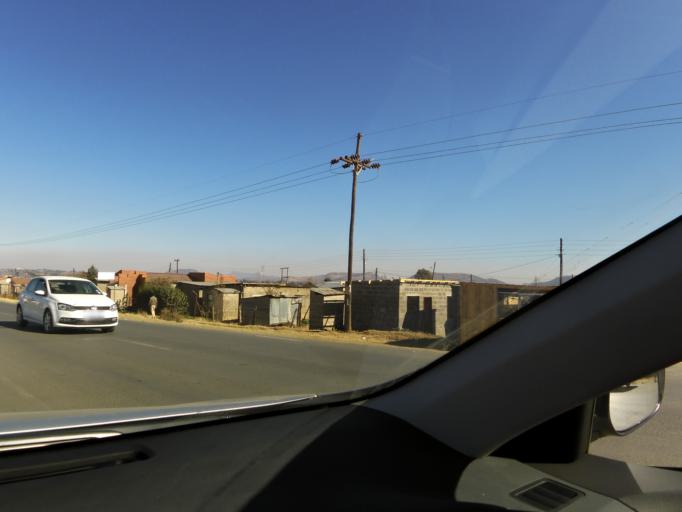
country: LS
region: Maseru
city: Maseru
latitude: -29.2879
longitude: 27.5235
